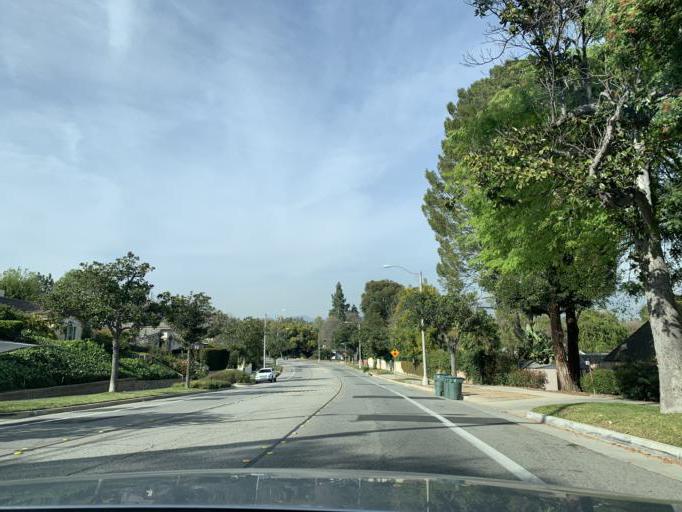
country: US
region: California
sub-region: Los Angeles County
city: South Pasadena
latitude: 34.1344
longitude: -118.1762
